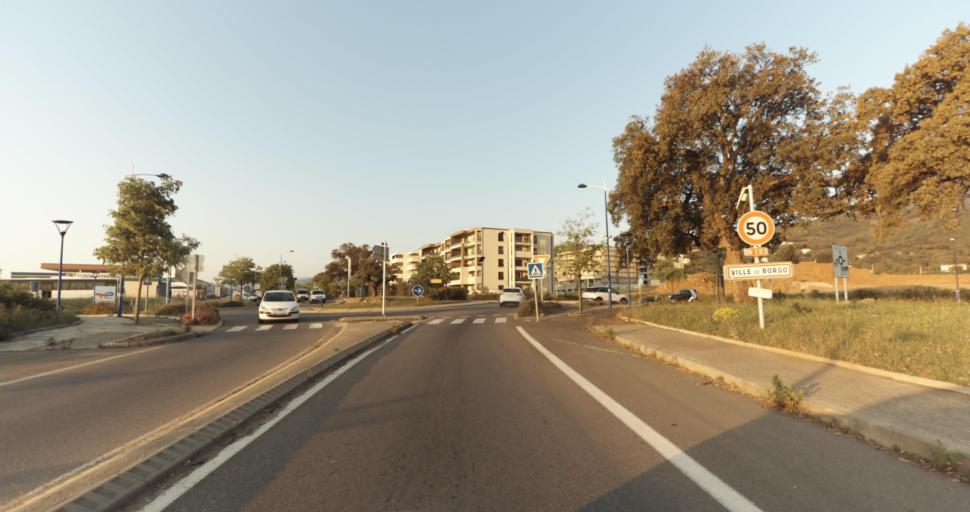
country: FR
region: Corsica
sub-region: Departement de la Haute-Corse
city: Borgo
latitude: 42.5690
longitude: 9.4408
